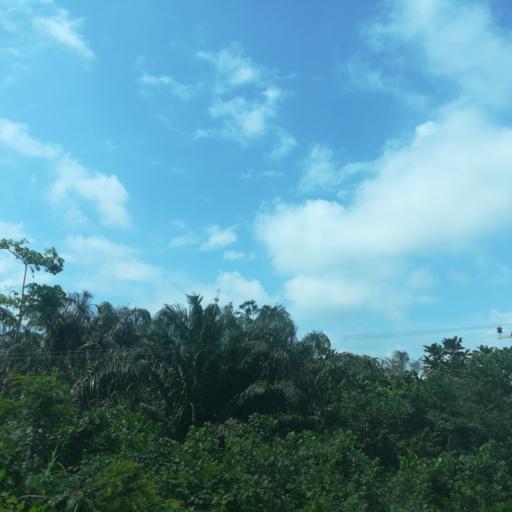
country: NG
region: Lagos
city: Ikorodu
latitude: 6.6569
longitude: 3.6882
